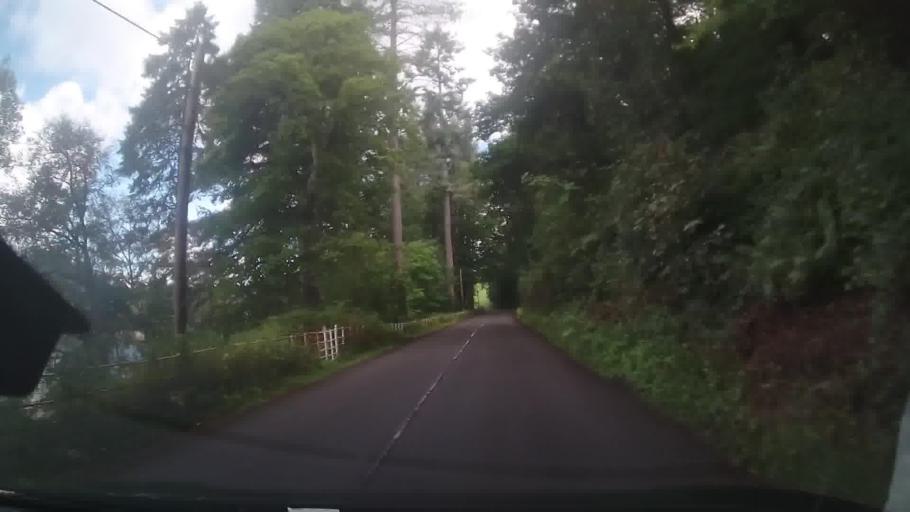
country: GB
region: Wales
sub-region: Sir Powys
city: Llangynog
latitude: 52.7653
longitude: -3.4535
